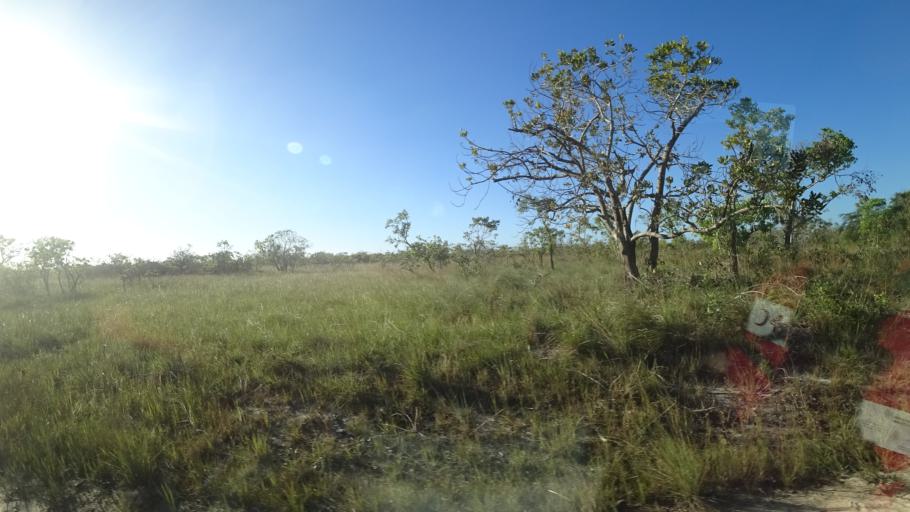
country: MZ
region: Sofala
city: Beira
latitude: -19.5753
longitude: 35.2166
